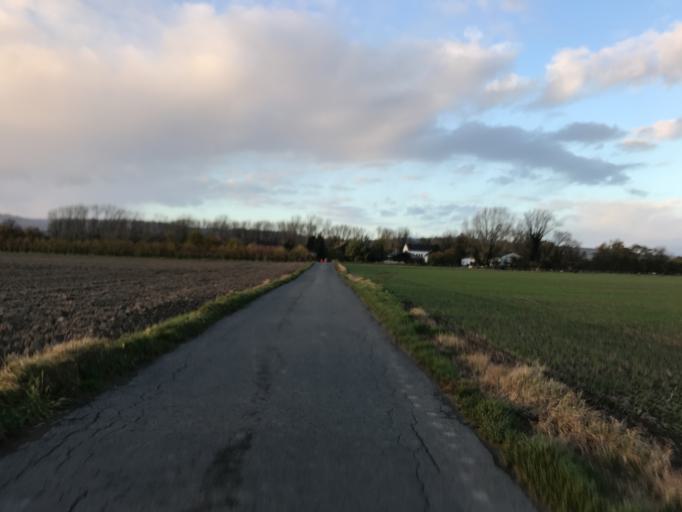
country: DE
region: Hesse
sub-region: Regierungsbezirk Darmstadt
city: Eltville
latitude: 50.0101
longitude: 8.1195
